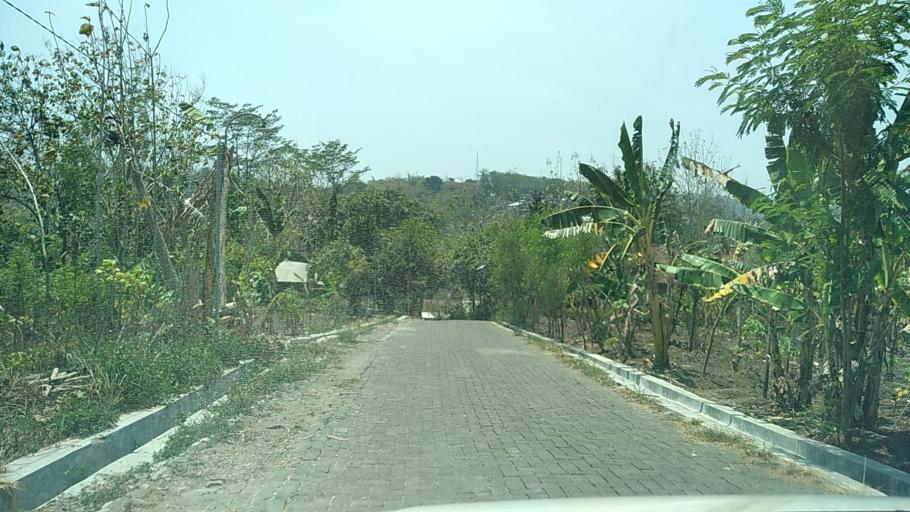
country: ID
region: Central Java
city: Semarang
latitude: -7.0306
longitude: 110.3764
